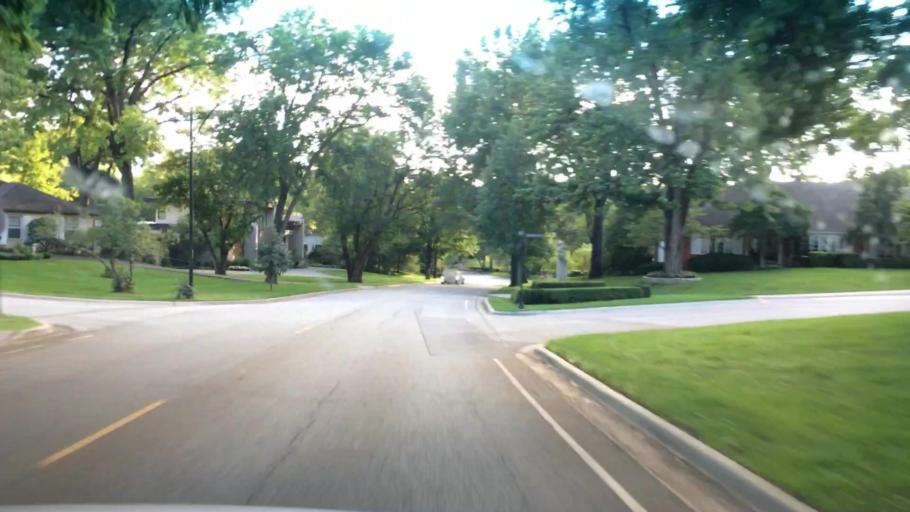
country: US
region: Kansas
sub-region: Johnson County
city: Mission Hills
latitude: 39.0114
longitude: -94.6181
